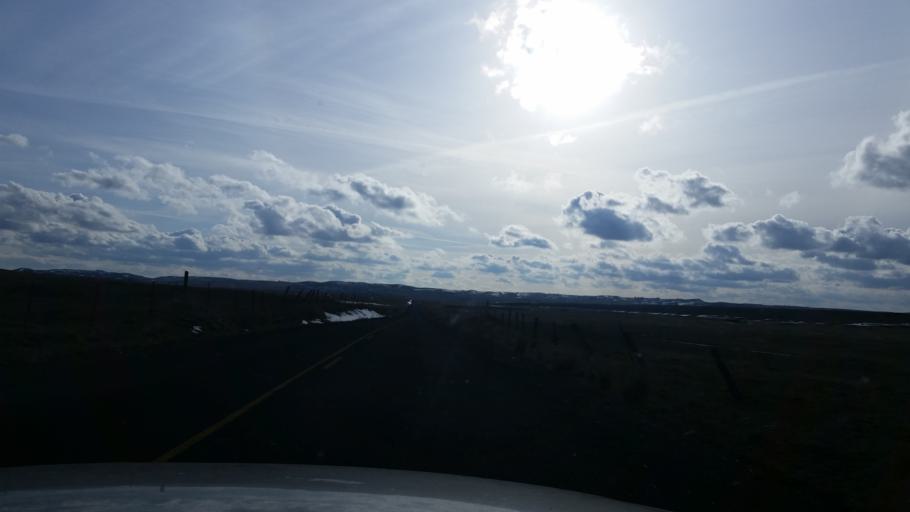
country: US
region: Washington
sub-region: Spokane County
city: Cheney
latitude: 47.2775
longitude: -117.6507
